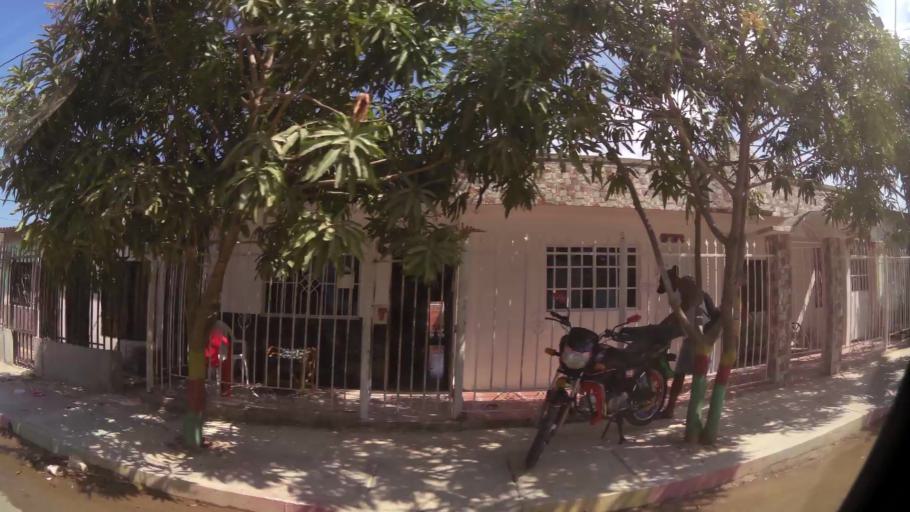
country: CO
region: Atlantico
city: Barranquilla
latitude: 10.9665
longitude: -74.8314
